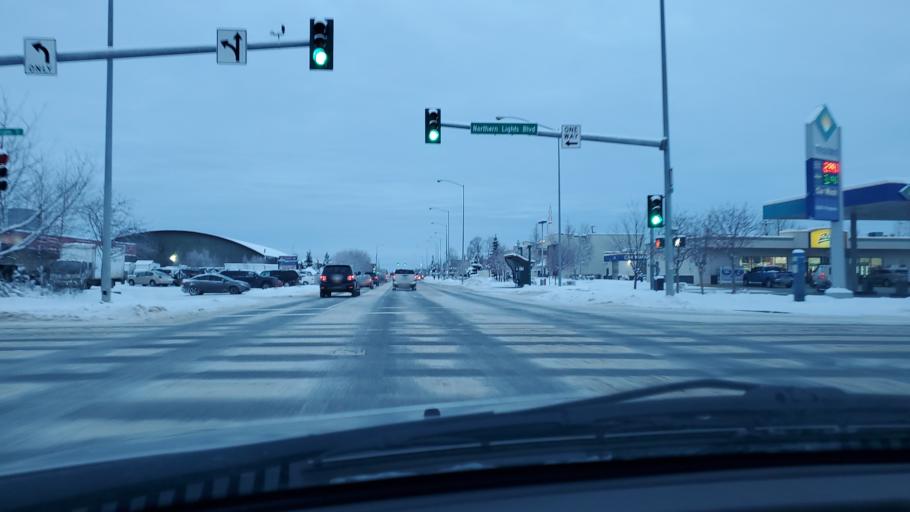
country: US
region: Alaska
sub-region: Anchorage Municipality
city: Anchorage
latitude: 61.1952
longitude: -149.8831
